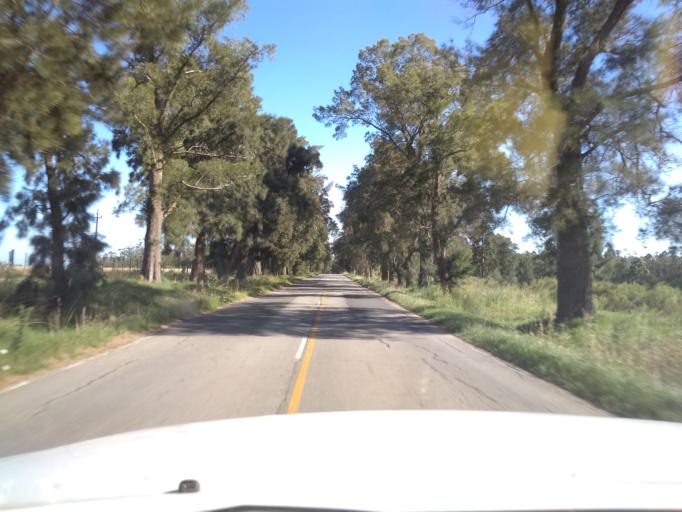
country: UY
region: Canelones
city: San Bautista
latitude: -34.3842
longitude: -55.9595
